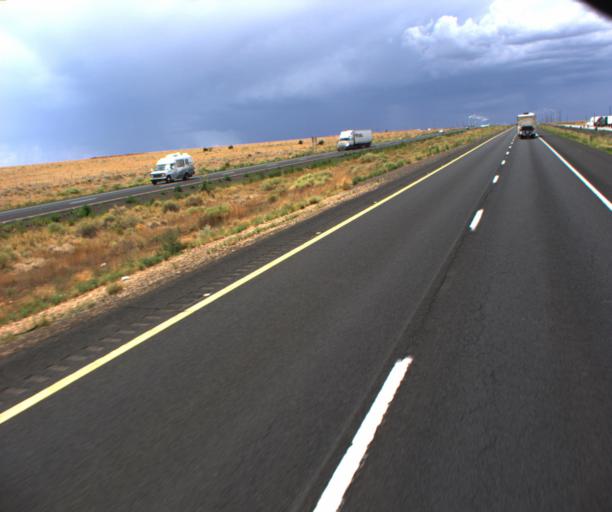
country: US
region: Arizona
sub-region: Coconino County
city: LeChee
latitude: 35.1027
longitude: -110.9908
